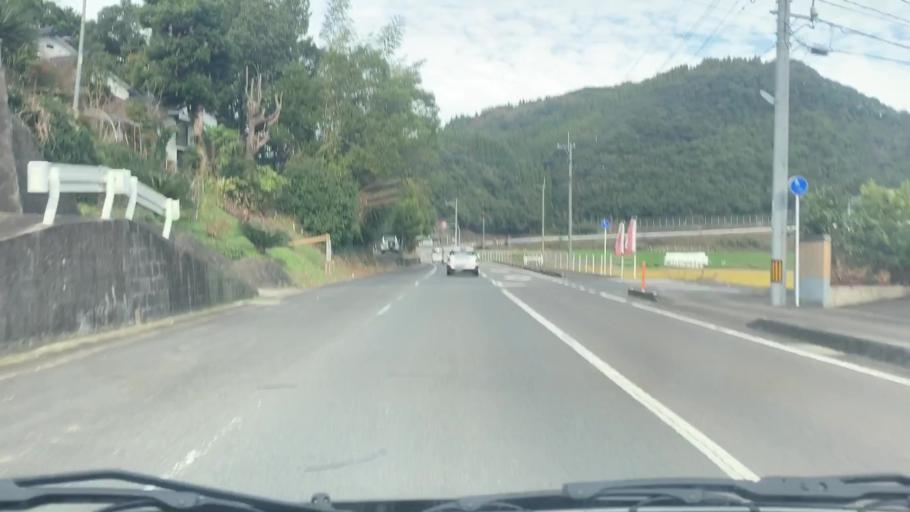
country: JP
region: Saga Prefecture
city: Imaricho-ko
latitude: 33.3252
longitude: 129.9689
